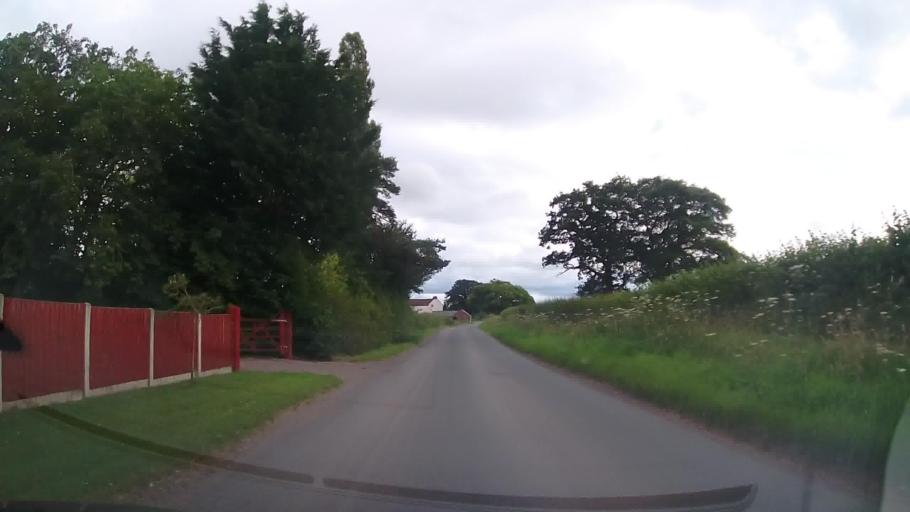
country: GB
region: England
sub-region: Shropshire
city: Wem
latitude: 52.8782
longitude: -2.7472
